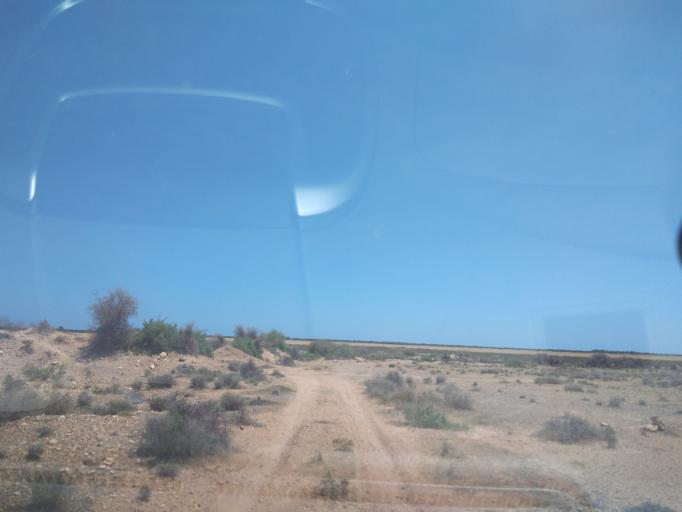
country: TN
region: Susah
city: Harqalah
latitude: 36.1696
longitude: 10.4490
